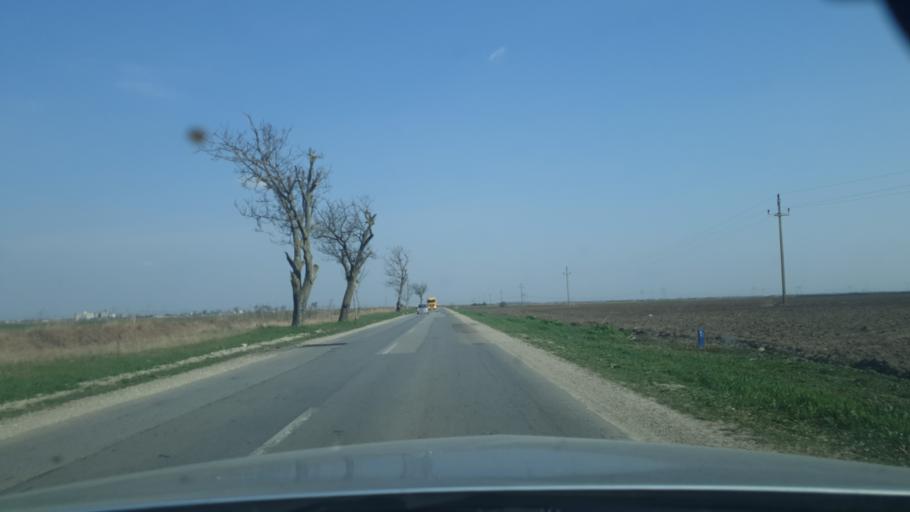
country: RS
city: Golubinci
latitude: 44.9802
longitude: 20.0882
